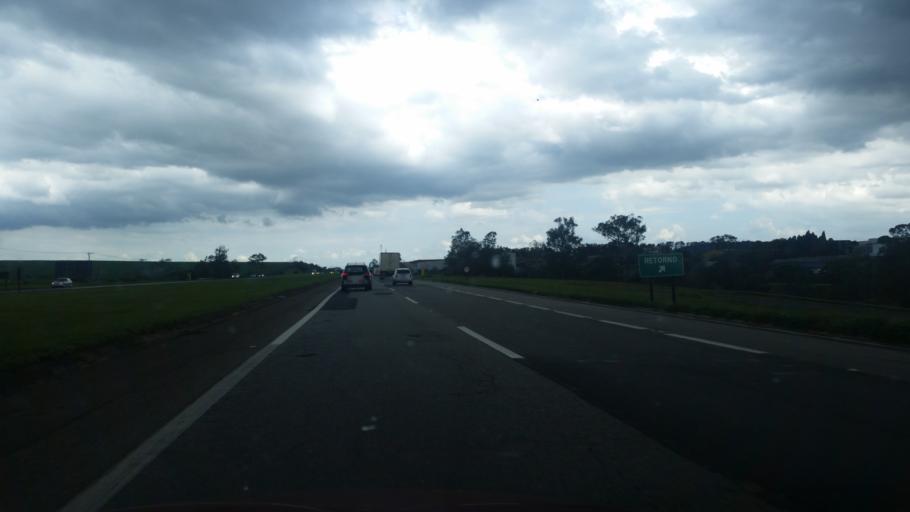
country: BR
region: Sao Paulo
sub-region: Porto Feliz
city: Porto Feliz
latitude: -23.3445
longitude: -47.5292
